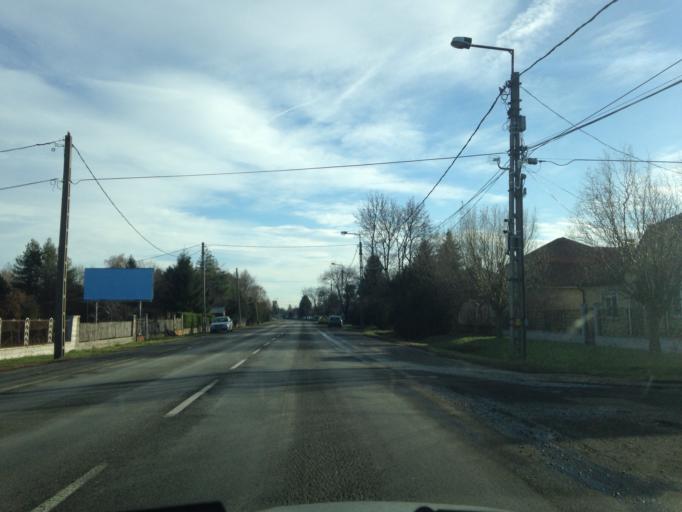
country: HU
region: Gyor-Moson-Sopron
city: Otteveny
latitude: 47.7323
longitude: 17.4802
